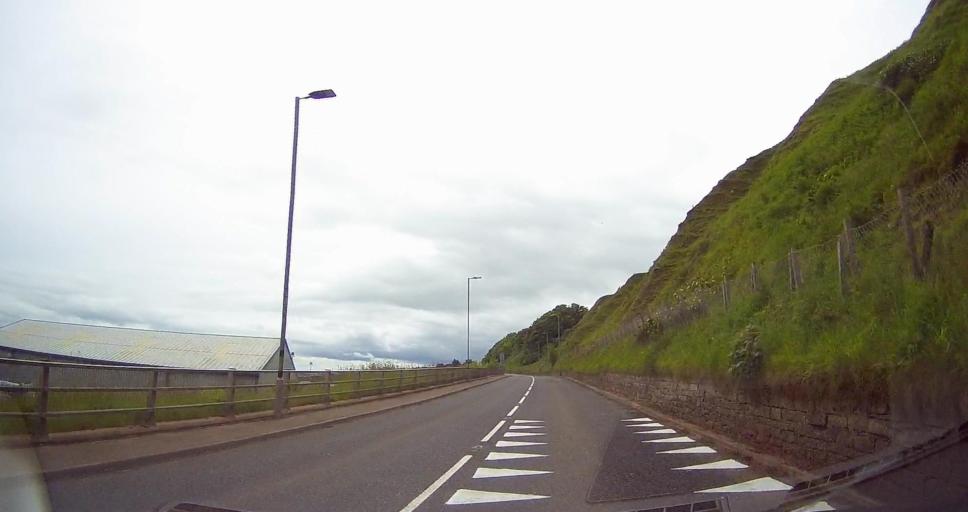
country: GB
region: Scotland
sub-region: Highland
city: Thurso
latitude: 58.6104
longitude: -3.5527
